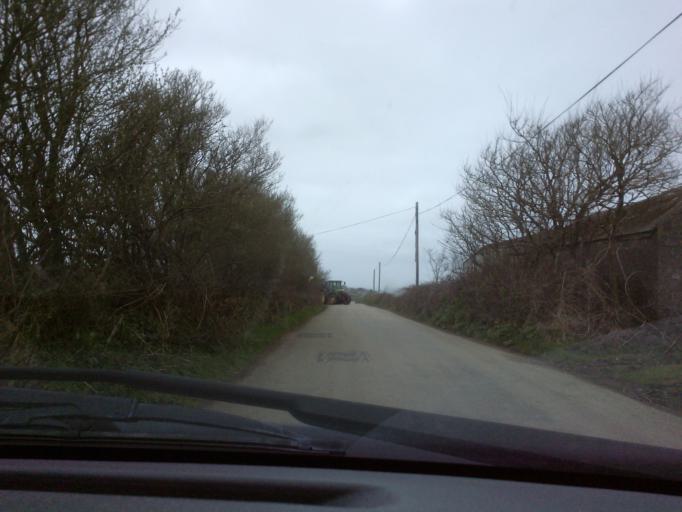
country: GB
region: England
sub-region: Cornwall
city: Saint Just
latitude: 50.1204
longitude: -5.6629
